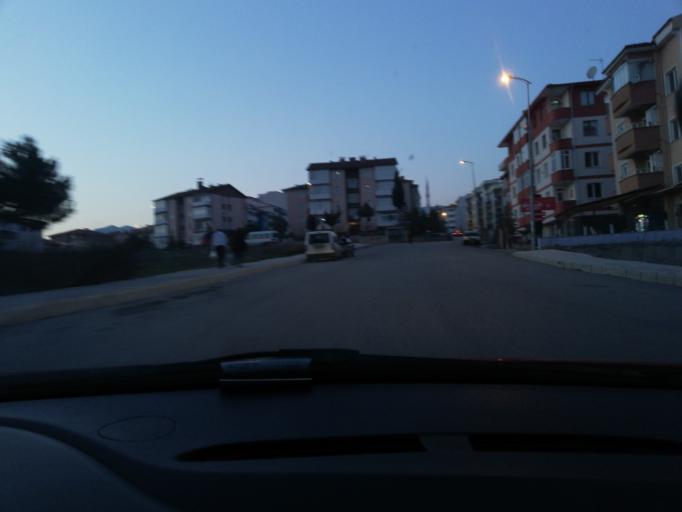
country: TR
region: Karabuk
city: Safranbolu
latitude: 41.2191
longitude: 32.6723
